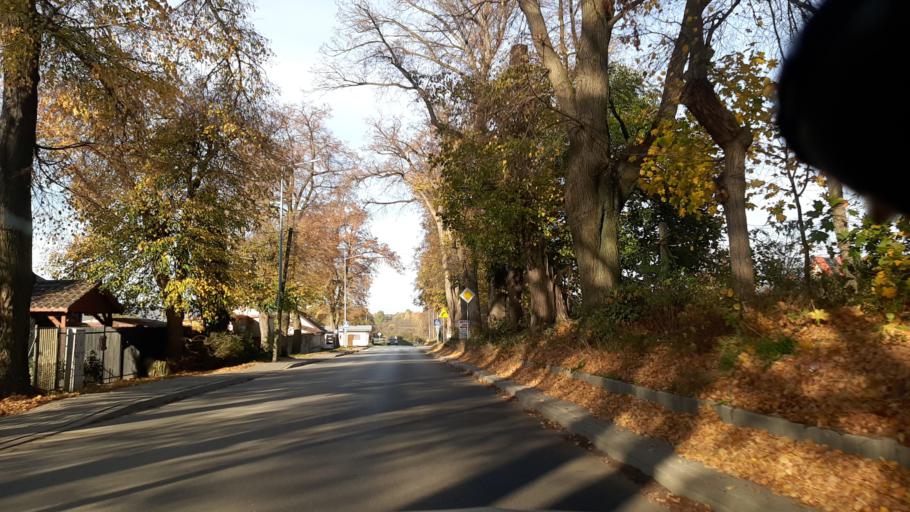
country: PL
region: Lublin Voivodeship
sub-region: Powiat lubelski
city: Lublin
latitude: 51.2882
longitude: 22.5750
